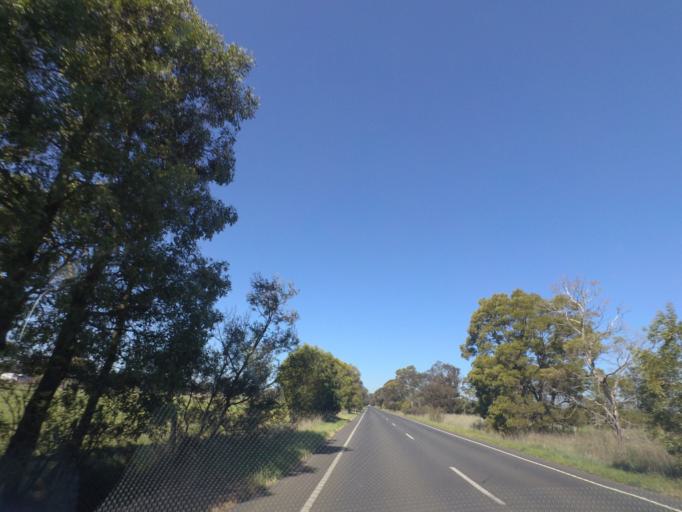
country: AU
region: Victoria
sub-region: Whittlesea
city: Whittlesea
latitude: -37.3271
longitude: 144.9749
